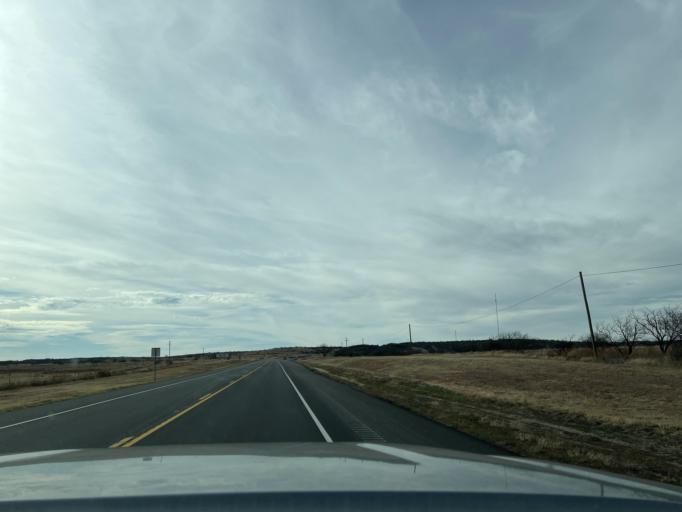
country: US
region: Texas
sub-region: Shackelford County
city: Albany
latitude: 32.7052
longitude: -99.4043
